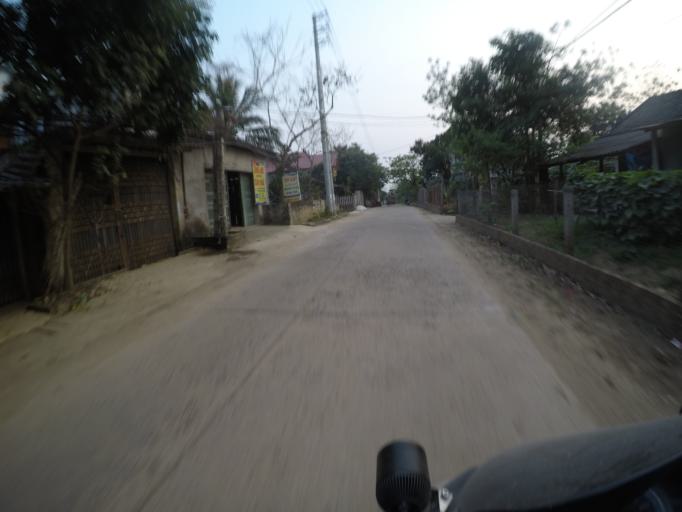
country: VN
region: Vinh Phuc
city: Trai Ngau
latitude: 21.4651
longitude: 105.5707
